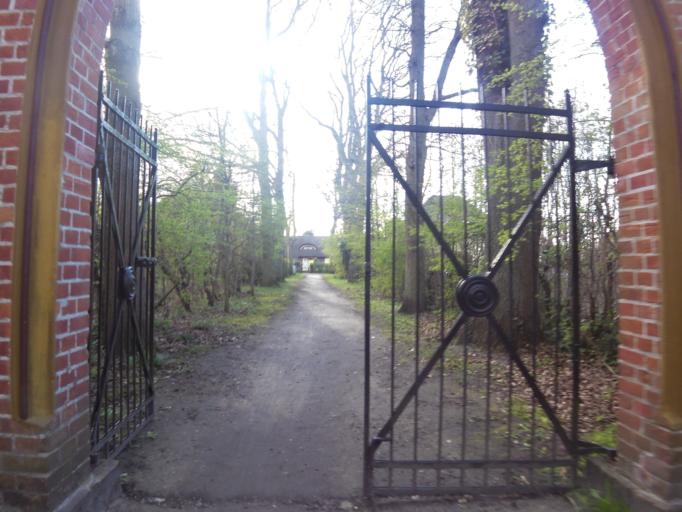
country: DE
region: Mecklenburg-Vorpommern
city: Zingst
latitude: 54.4374
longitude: 12.6884
